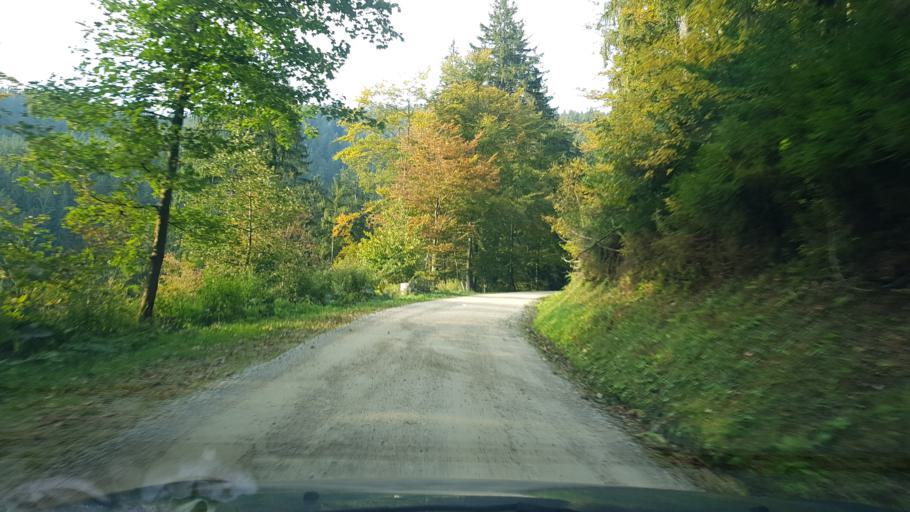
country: SI
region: Slovenj Gradec
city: Legen
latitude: 46.5222
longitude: 15.1358
